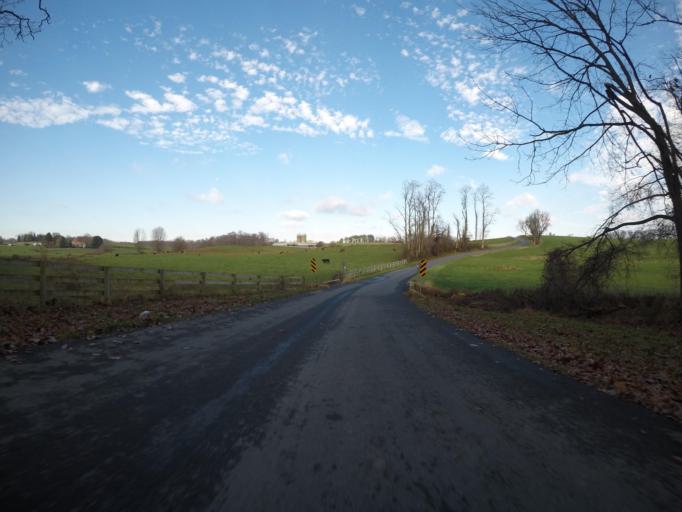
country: US
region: Maryland
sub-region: Carroll County
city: Hampstead
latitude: 39.5542
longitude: -76.8130
